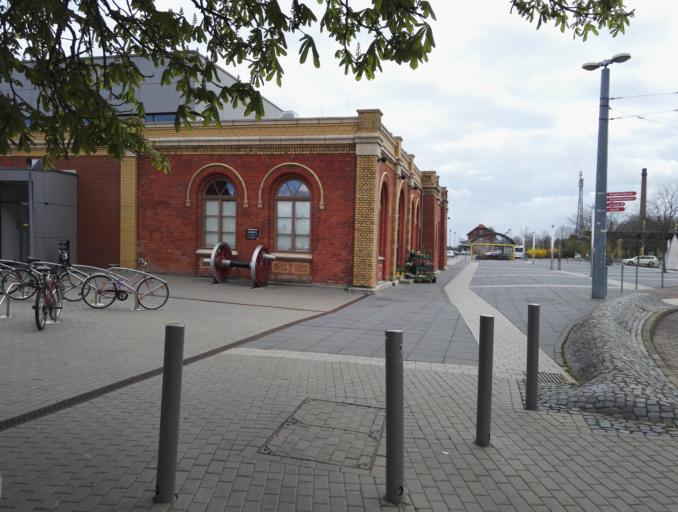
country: DE
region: Saxony-Anhalt
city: Halberstadt
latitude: 51.8991
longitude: 11.0723
